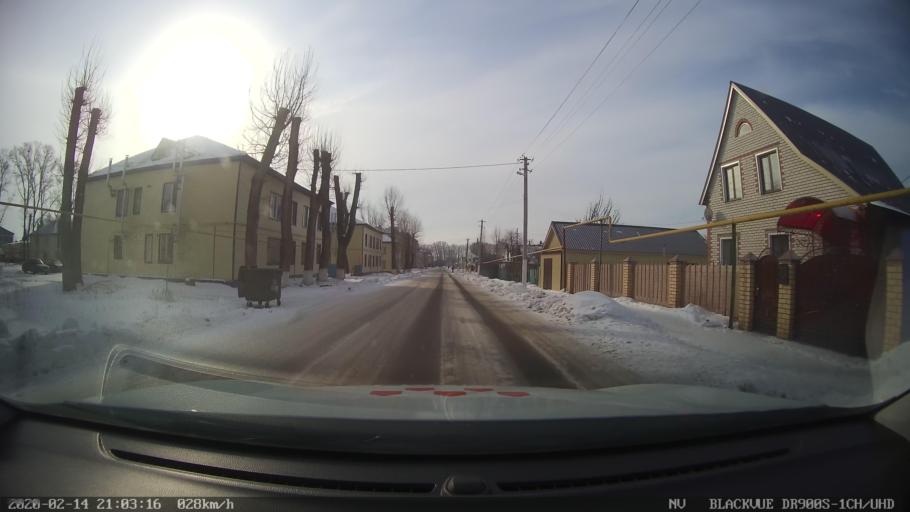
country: RU
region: Tatarstan
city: Kuybyshevskiy Zaton
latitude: 55.1574
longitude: 49.1764
